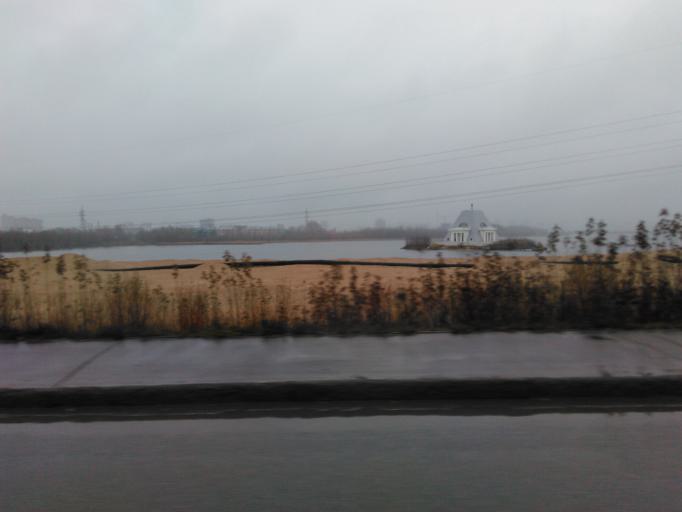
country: RU
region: Tatarstan
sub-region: Gorod Kazan'
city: Kazan
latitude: 55.7993
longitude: 49.0737
